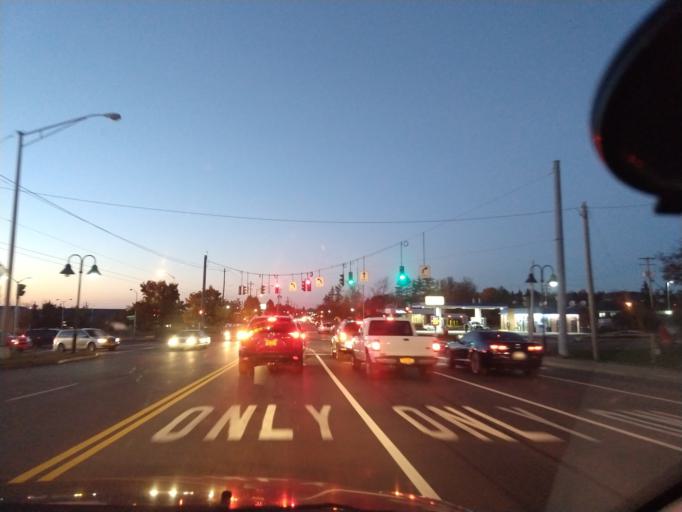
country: US
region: New York
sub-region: Tompkins County
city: Lansing
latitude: 42.4825
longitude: -76.4848
